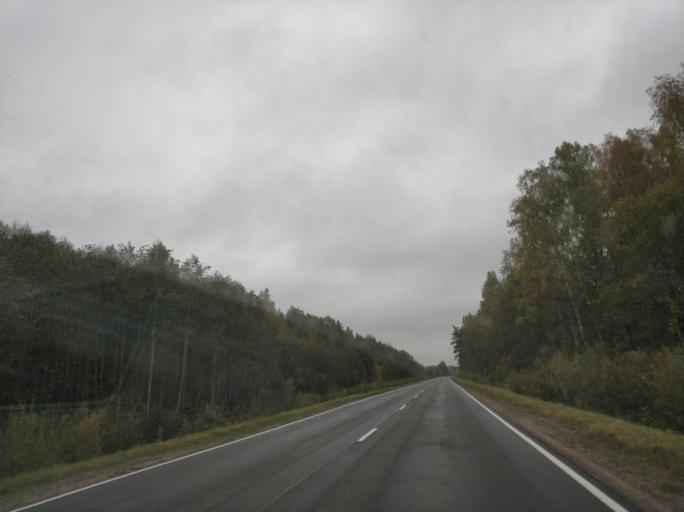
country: BY
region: Vitebsk
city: Rasony
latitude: 56.0926
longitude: 28.7211
